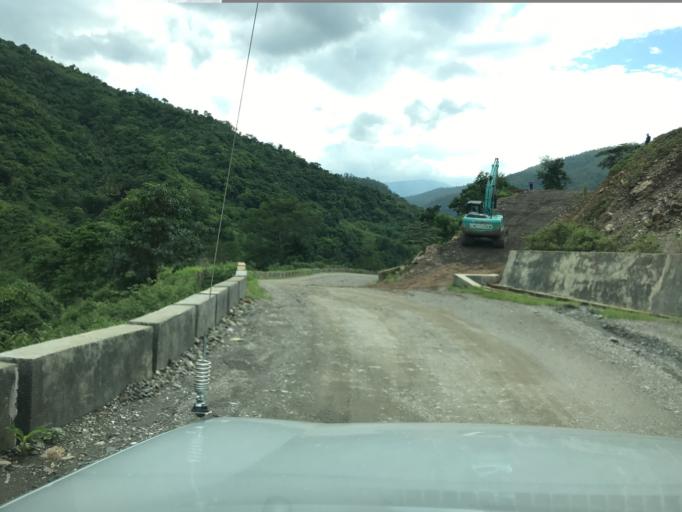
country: TL
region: Aileu
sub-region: Aileu Villa
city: Aileu
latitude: -8.6420
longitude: 125.5130
